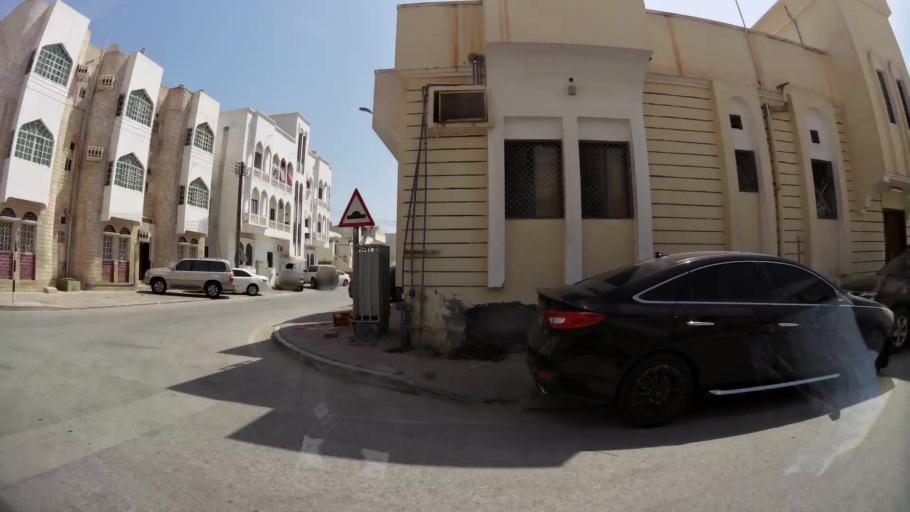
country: OM
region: Zufar
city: Salalah
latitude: 17.0088
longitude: 54.0699
